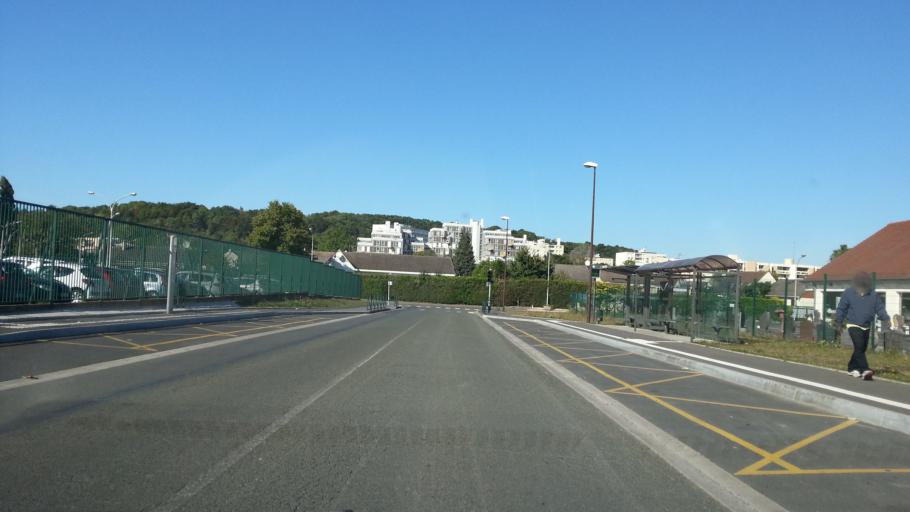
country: FR
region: Picardie
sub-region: Departement de l'Oise
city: Nogent-sur-Oise
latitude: 49.2654
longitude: 2.4632
